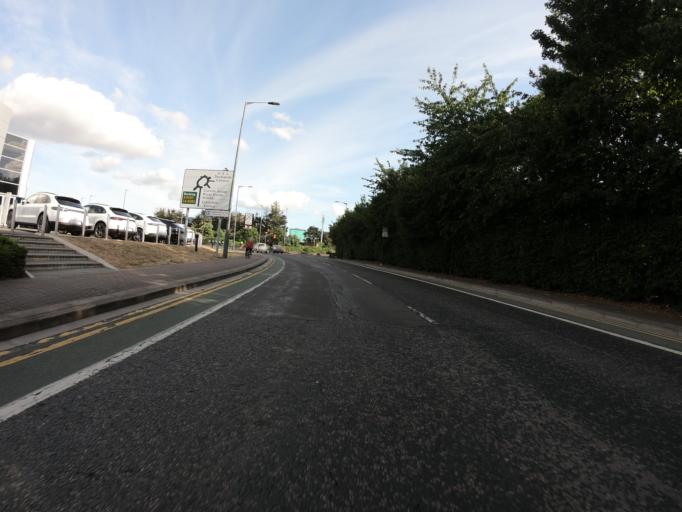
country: GB
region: England
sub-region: Greater London
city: Woolwich
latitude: 51.5095
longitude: 0.0701
